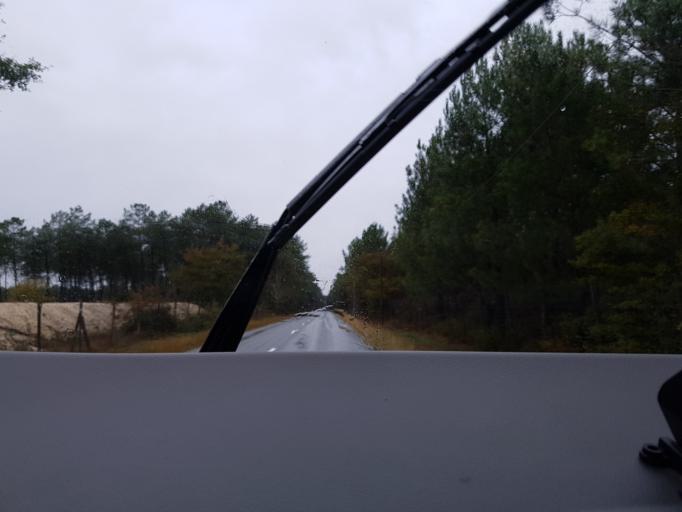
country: FR
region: Aquitaine
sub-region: Departement de la Gironde
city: Belin-Beliet
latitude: 44.5129
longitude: -0.7436
